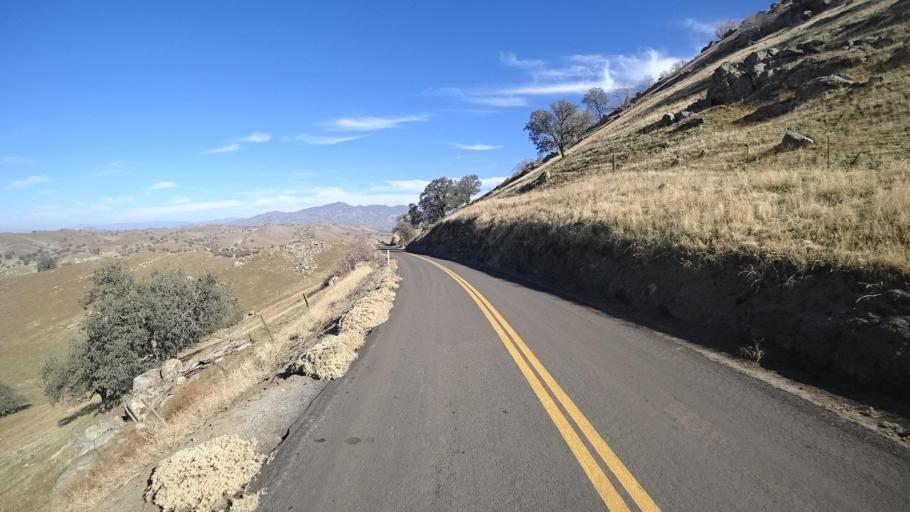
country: US
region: California
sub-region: Tulare County
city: Richgrove
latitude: 35.6939
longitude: -118.8646
